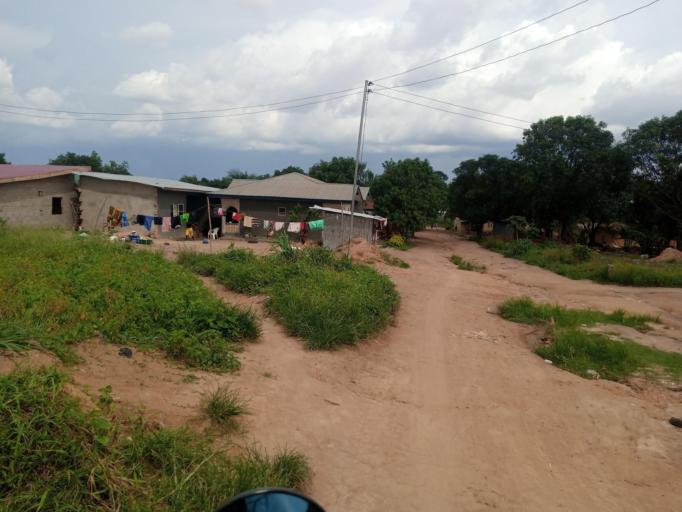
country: SL
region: Southern Province
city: Bo
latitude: 7.9824
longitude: -11.7432
